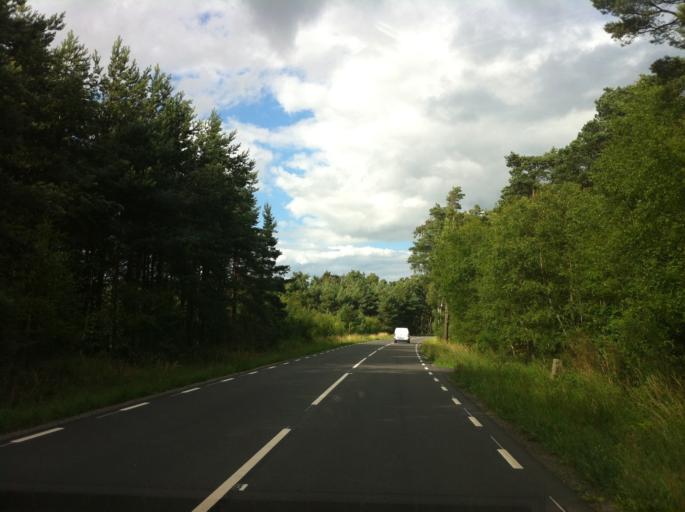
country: SE
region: Skane
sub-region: Ystads Kommun
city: Kopingebro
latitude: 55.3941
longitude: 14.1633
